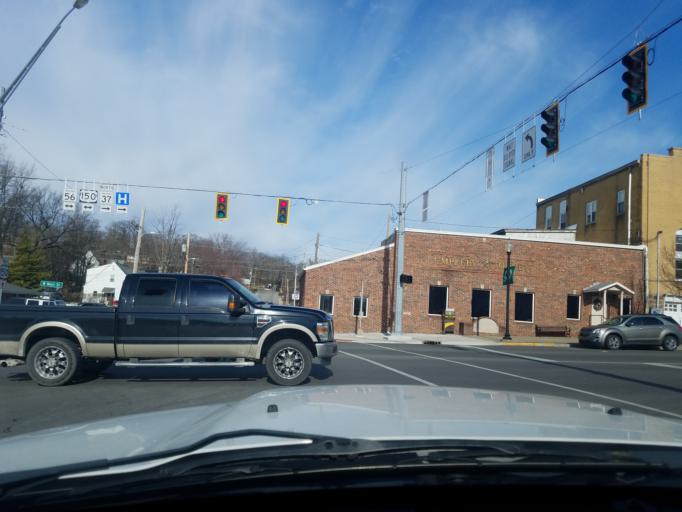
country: US
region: Indiana
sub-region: Orange County
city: Paoli
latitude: 38.5560
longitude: -86.4697
